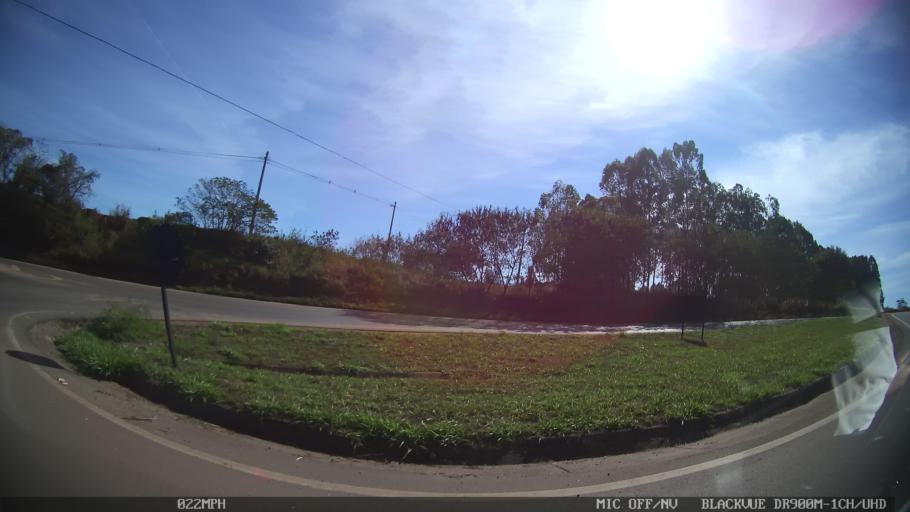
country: BR
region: Sao Paulo
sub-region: Pirassununga
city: Pirassununga
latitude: -22.0411
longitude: -47.4371
